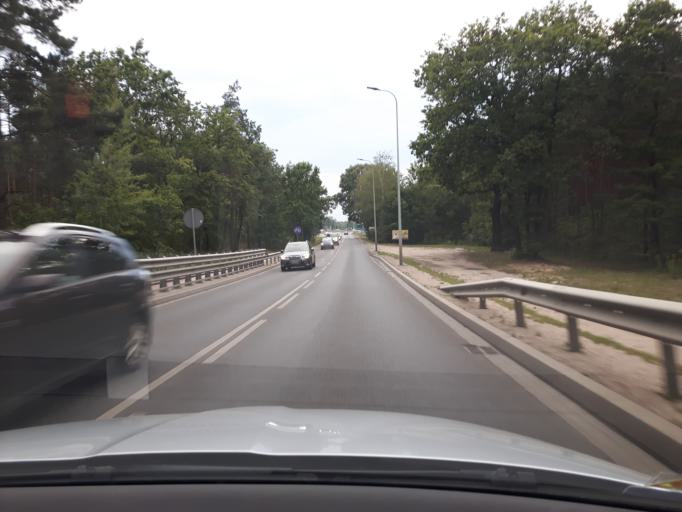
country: PL
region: Masovian Voivodeship
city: Zielonka
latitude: 52.2971
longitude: 21.1448
